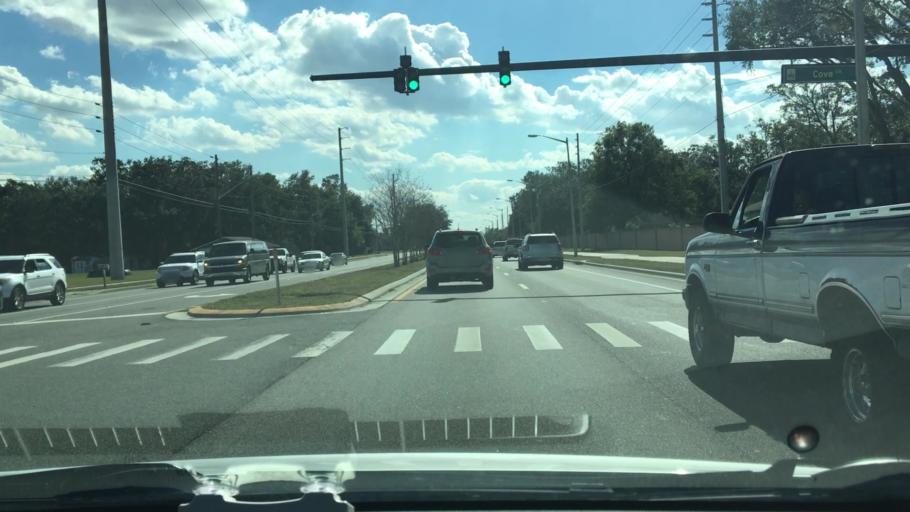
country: US
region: Florida
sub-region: Orange County
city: Conway
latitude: 28.4732
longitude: -81.3308
